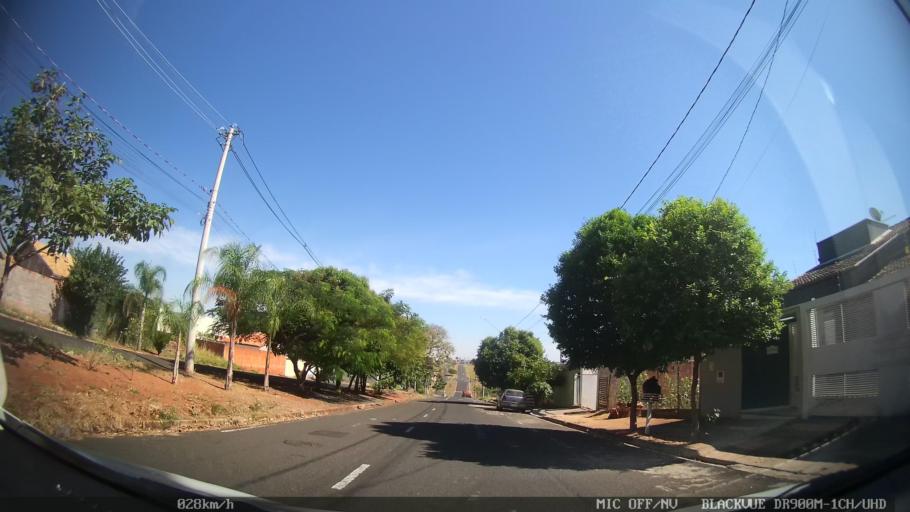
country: BR
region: Sao Paulo
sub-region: Sao Jose Do Rio Preto
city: Sao Jose do Rio Preto
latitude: -20.7664
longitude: -49.4151
